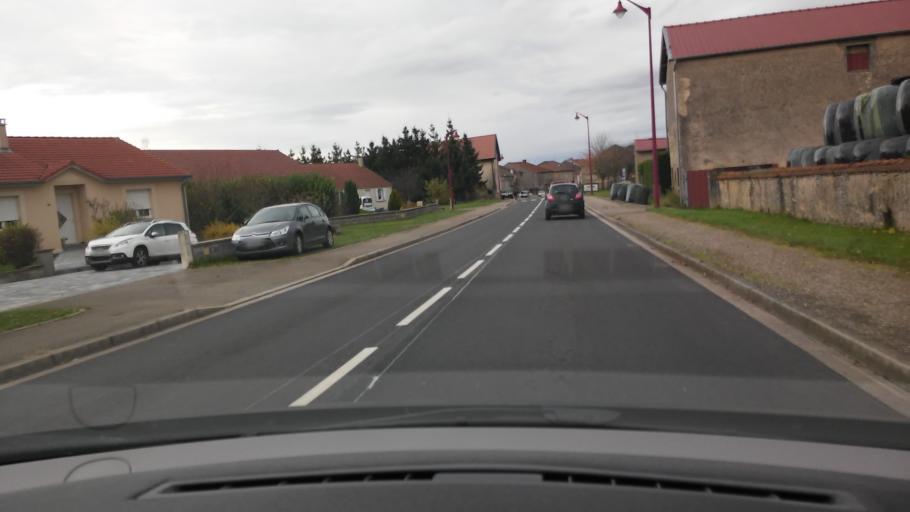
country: FR
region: Lorraine
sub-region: Departement de la Moselle
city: Boulay-Moselle
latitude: 49.1665
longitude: 6.4454
